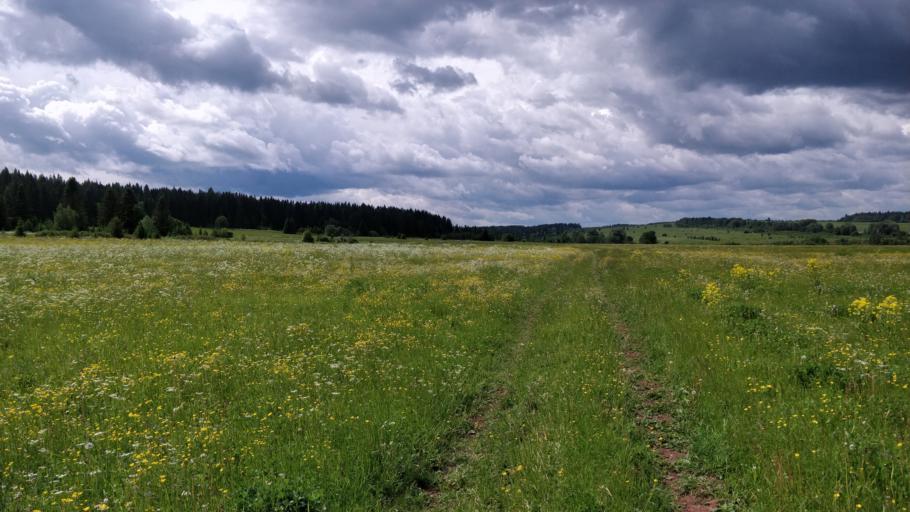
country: RU
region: Perm
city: Ust'-Kachka
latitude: 57.9436
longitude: 55.6973
